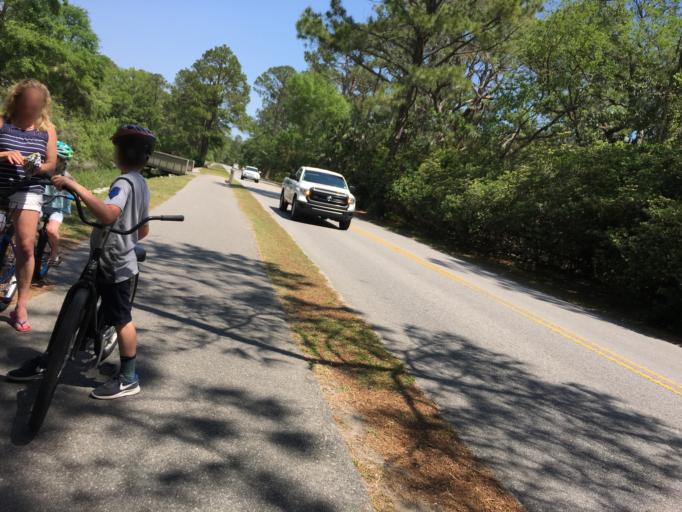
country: US
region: South Carolina
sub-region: Beaufort County
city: Hilton Head Island
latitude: 32.1162
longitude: -80.8077
